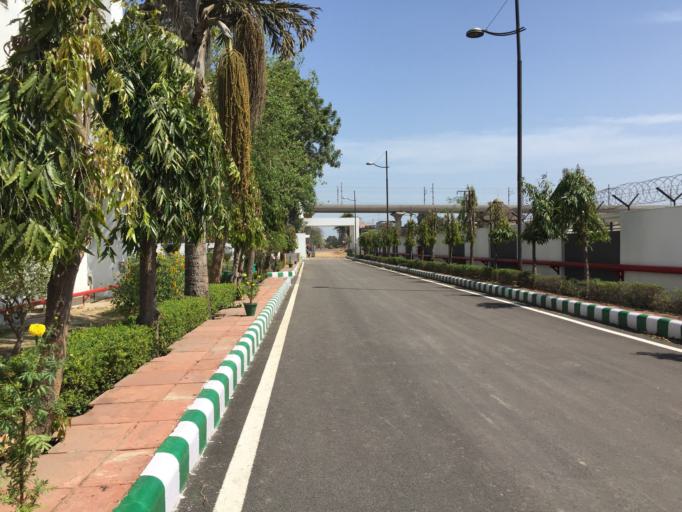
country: IN
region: Haryana
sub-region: Faridabad District
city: Faridabad
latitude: 28.4564
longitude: 77.3057
